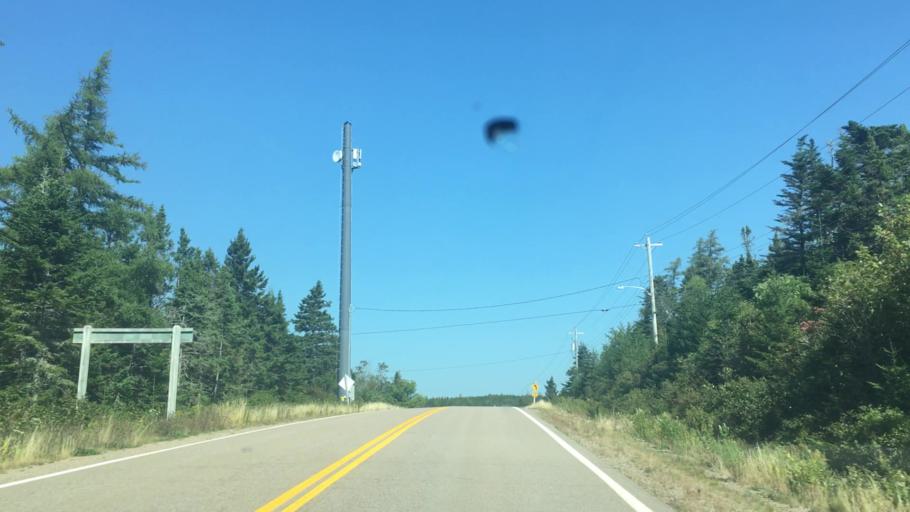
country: CA
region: Nova Scotia
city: Antigonish
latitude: 45.0248
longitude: -62.0313
